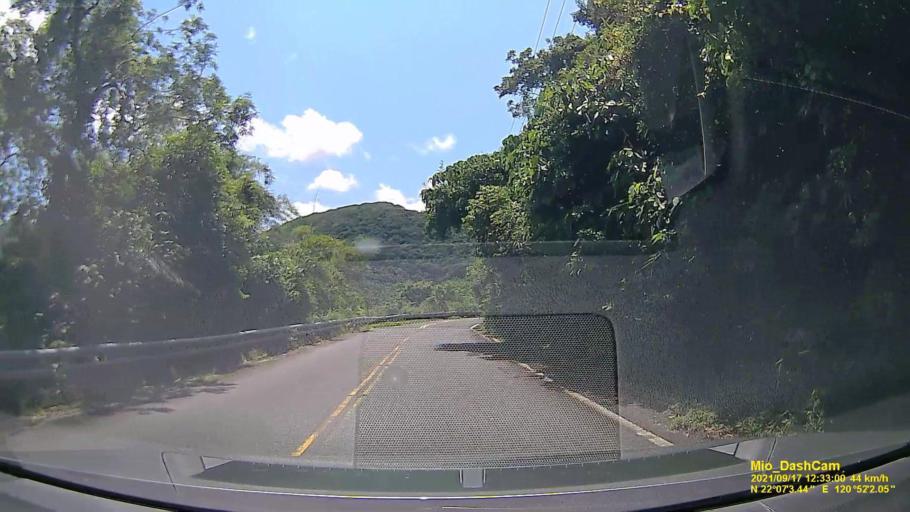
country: TW
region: Taiwan
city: Hengchun
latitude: 22.1176
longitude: 120.8672
